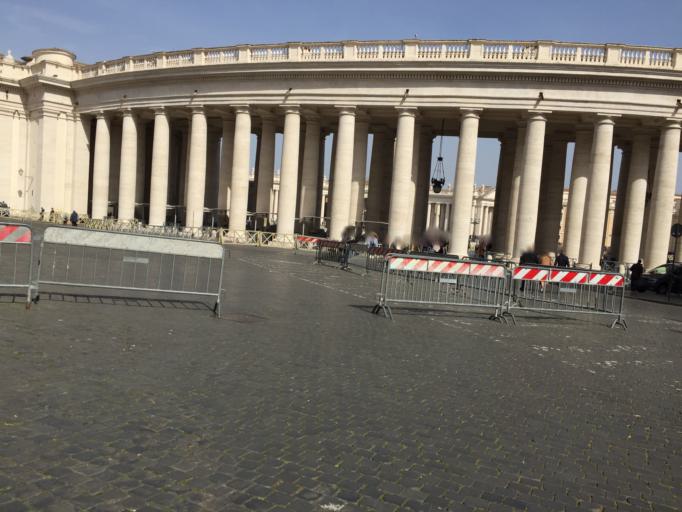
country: VA
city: Vatican City
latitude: 41.9010
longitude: 12.4564
